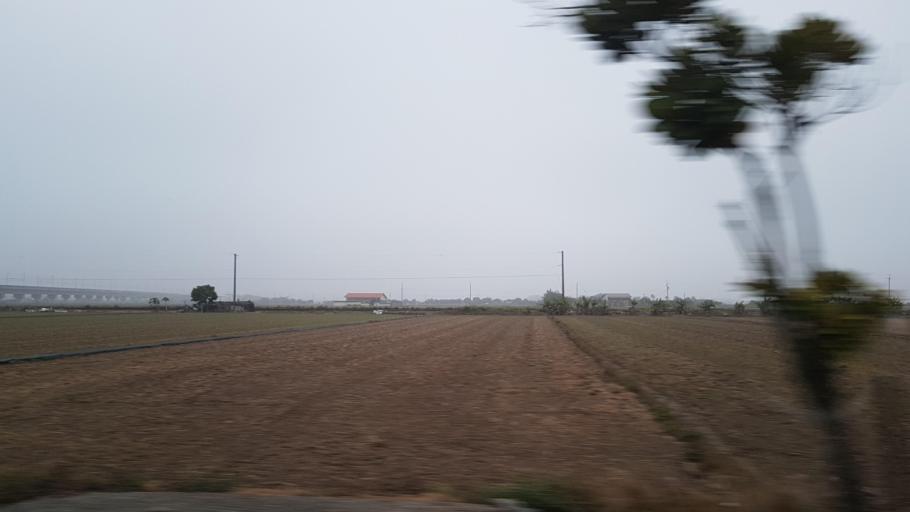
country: TW
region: Taiwan
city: Xinying
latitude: 23.3420
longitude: 120.3348
